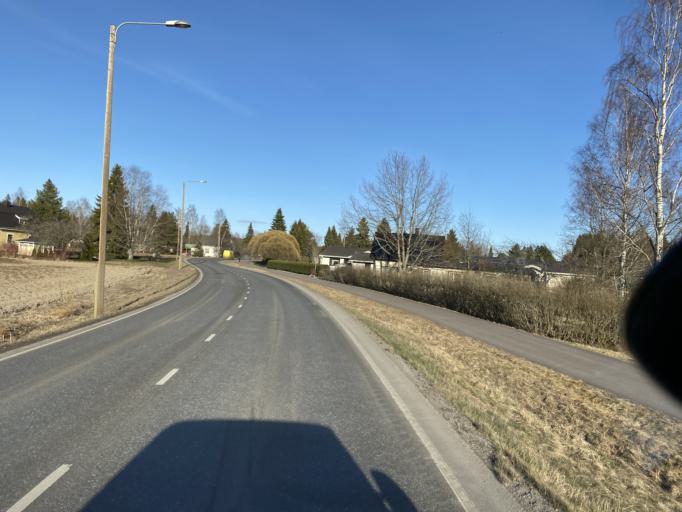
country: FI
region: Satakunta
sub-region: Pori
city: Huittinen
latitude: 61.1798
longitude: 22.7258
